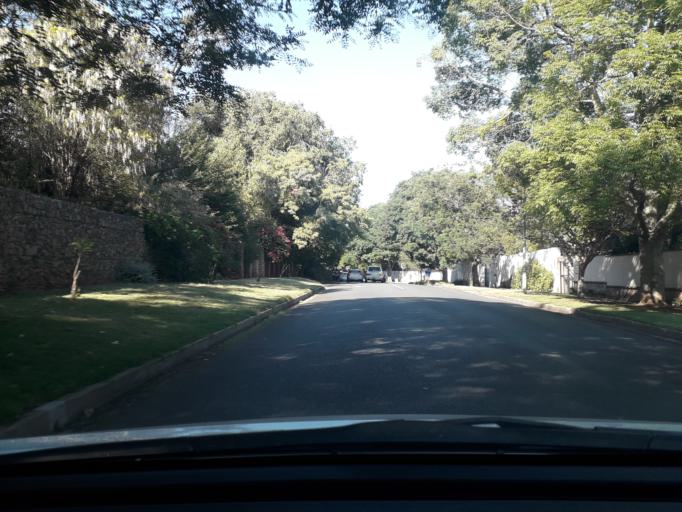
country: ZA
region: Gauteng
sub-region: City of Johannesburg Metropolitan Municipality
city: Johannesburg
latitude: -26.1675
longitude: 28.0254
